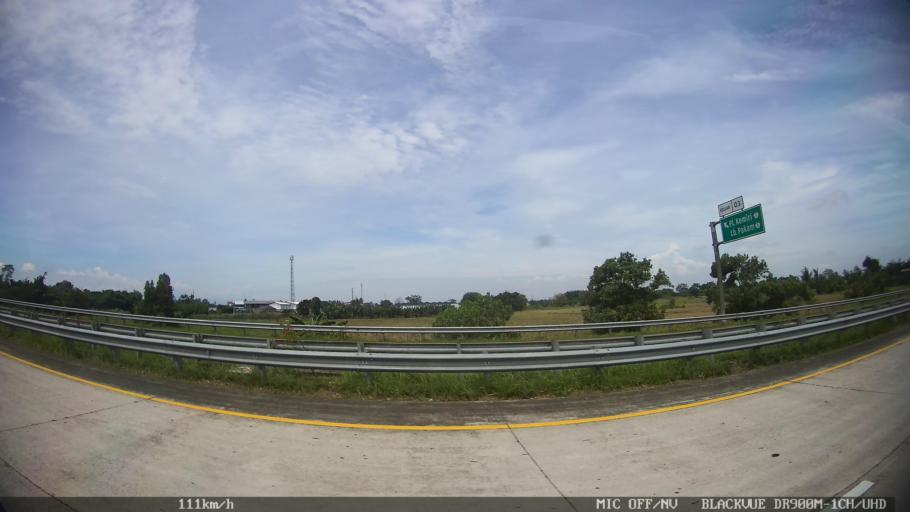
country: ID
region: North Sumatra
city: Percut
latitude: 3.5551
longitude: 98.8522
